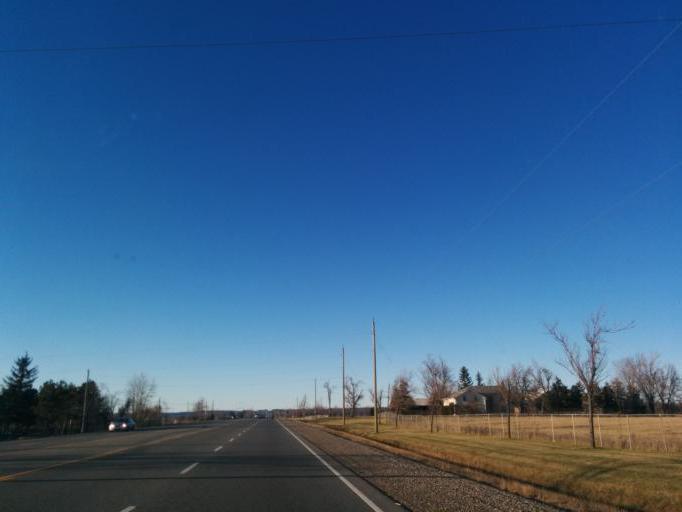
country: CA
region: Ontario
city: Brampton
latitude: 43.7820
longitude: -79.8895
